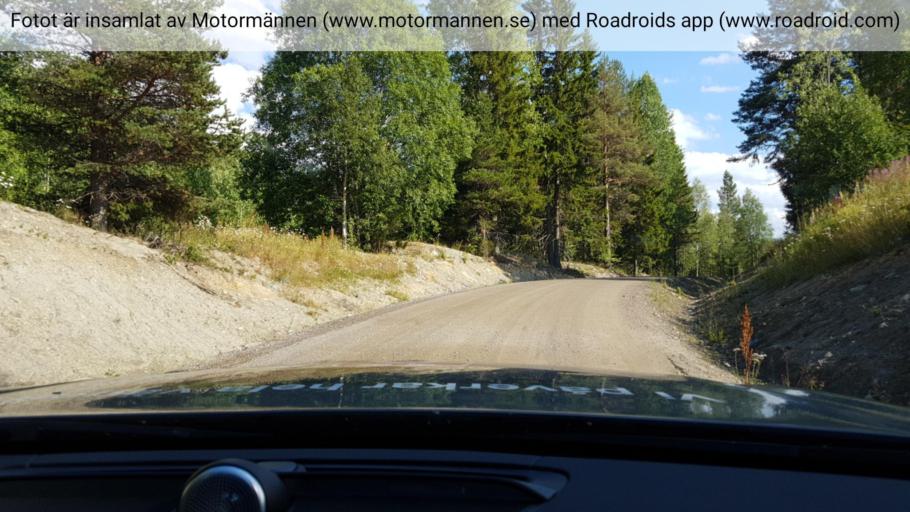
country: SE
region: Jaemtland
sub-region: Stroemsunds Kommun
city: Stroemsund
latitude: 63.9902
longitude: 16.0051
